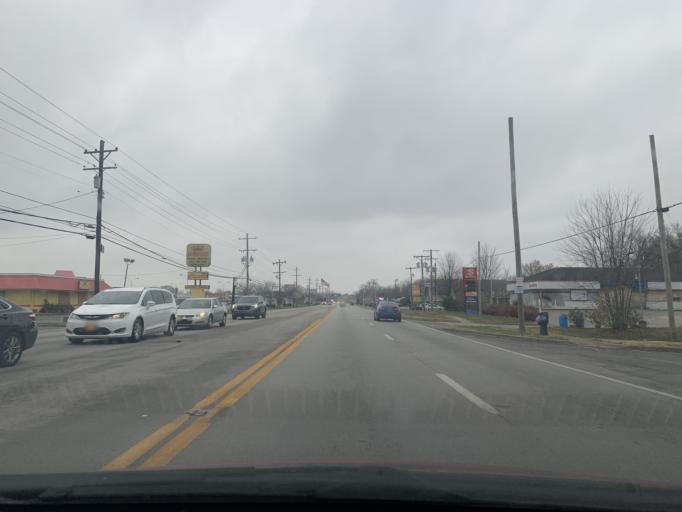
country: US
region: Kentucky
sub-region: Jefferson County
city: Okolona
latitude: 38.1685
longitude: -85.7063
